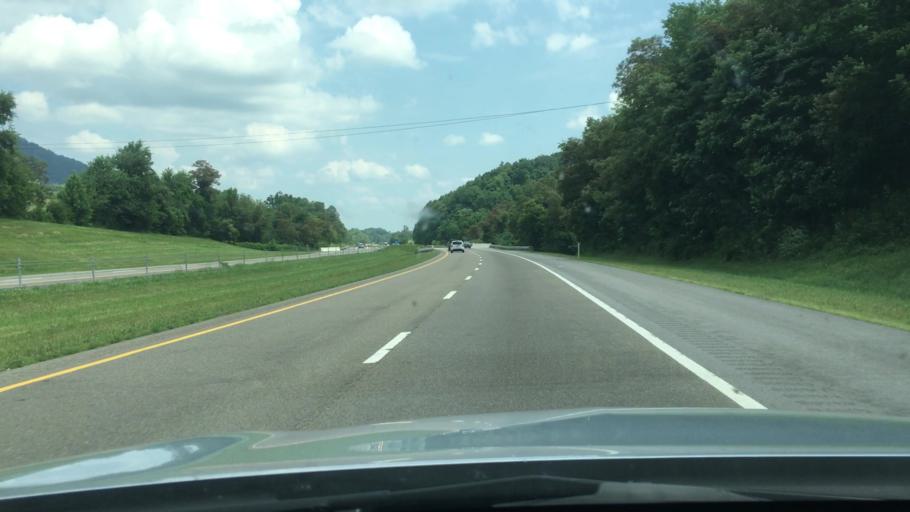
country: US
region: Tennessee
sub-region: Unicoi County
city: Unicoi
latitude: 36.2394
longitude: -82.3277
